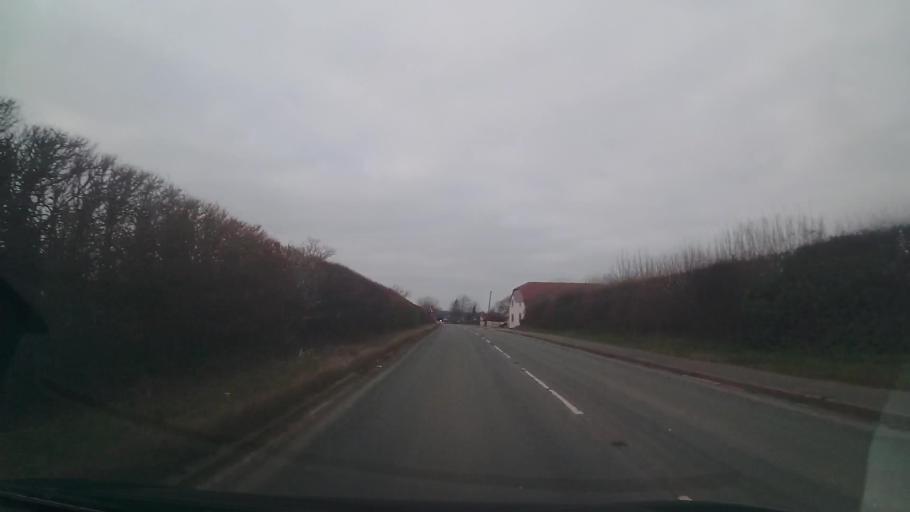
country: GB
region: England
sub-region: Shropshire
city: Bicton
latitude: 52.7245
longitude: -2.8121
